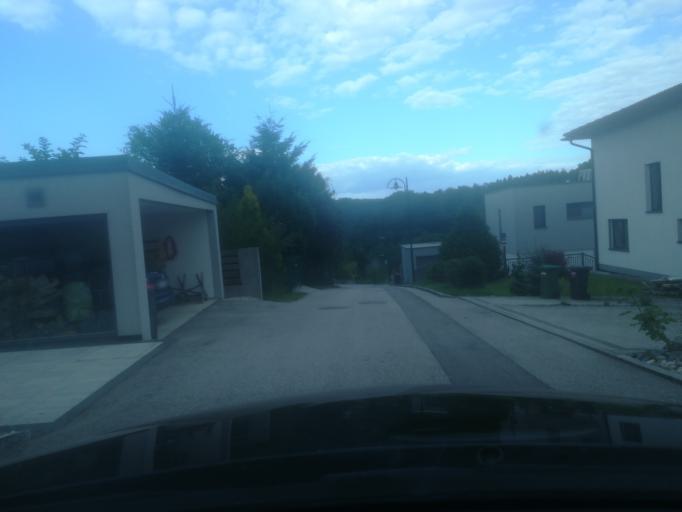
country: AT
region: Upper Austria
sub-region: Politischer Bezirk Urfahr-Umgebung
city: Ottensheim
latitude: 48.3215
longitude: 14.1863
